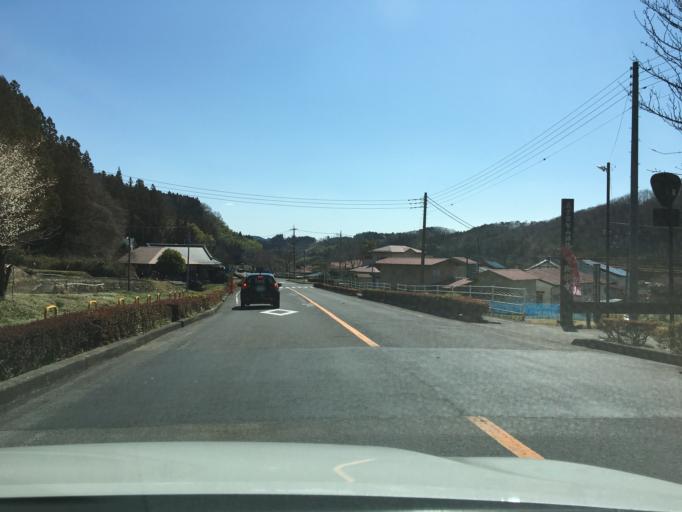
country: JP
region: Tochigi
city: Kuroiso
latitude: 37.0373
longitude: 140.1720
